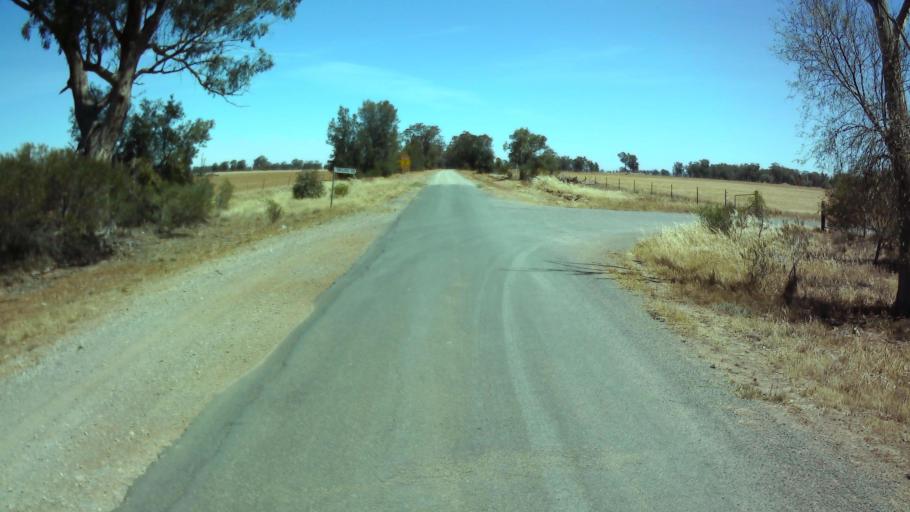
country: AU
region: New South Wales
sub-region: Weddin
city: Grenfell
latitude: -33.9063
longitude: 147.6854
